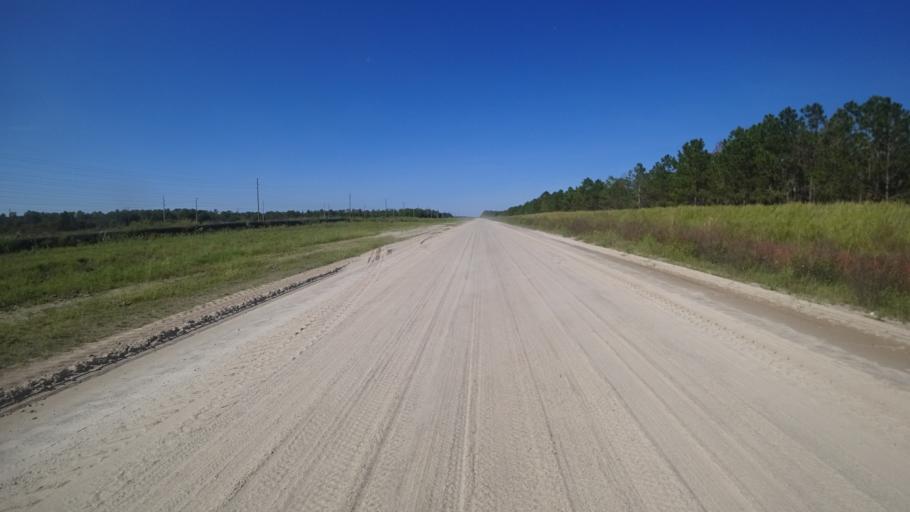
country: US
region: Florida
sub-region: Hillsborough County
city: Balm
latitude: 27.6487
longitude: -82.0952
